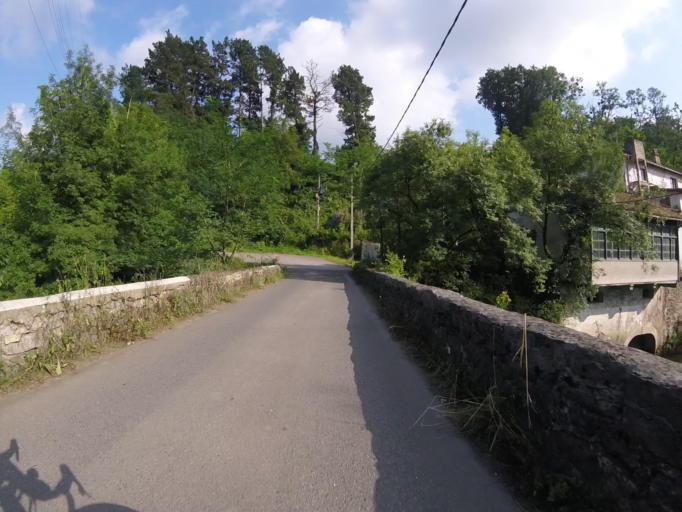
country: ES
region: Basque Country
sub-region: Provincia de Guipuzcoa
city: Astigarraga
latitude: 43.2592
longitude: -1.9532
